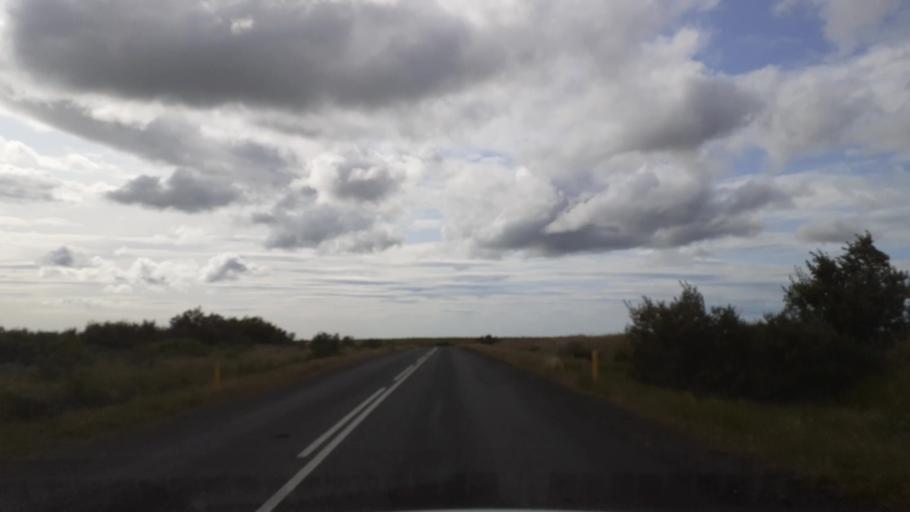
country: IS
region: South
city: Vestmannaeyjar
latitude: 63.8284
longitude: -20.4260
